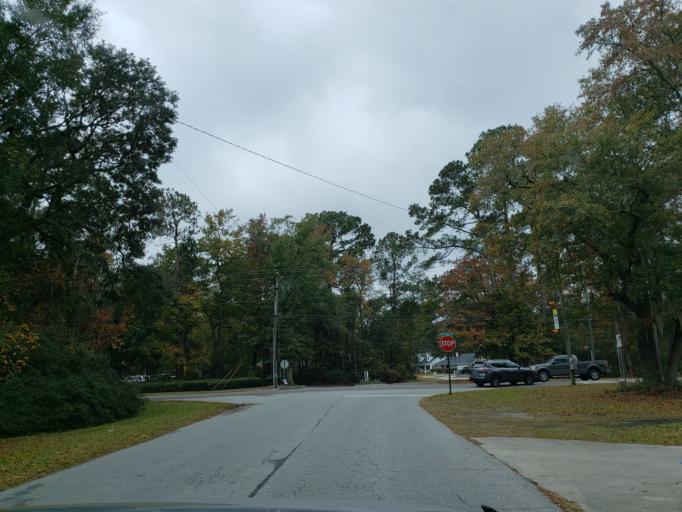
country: US
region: Georgia
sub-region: Chatham County
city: Wilmington Island
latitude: 32.0094
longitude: -80.9724
